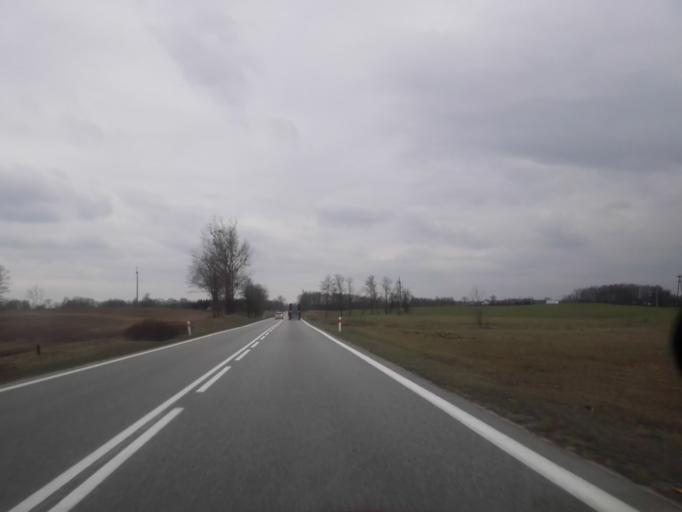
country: PL
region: Podlasie
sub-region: Powiat augustowski
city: Augustow
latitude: 53.8081
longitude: 22.9051
